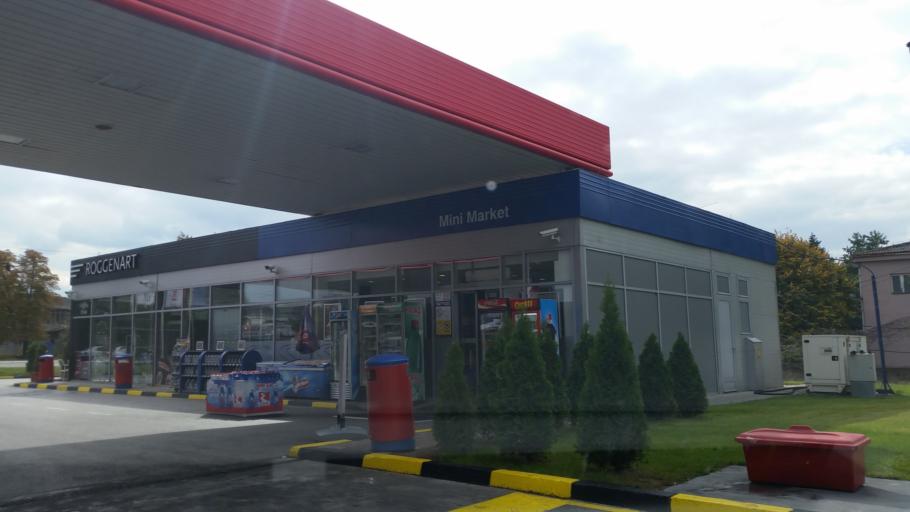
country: RS
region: Central Serbia
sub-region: Belgrade
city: Zemun
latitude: 44.8129
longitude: 20.3894
